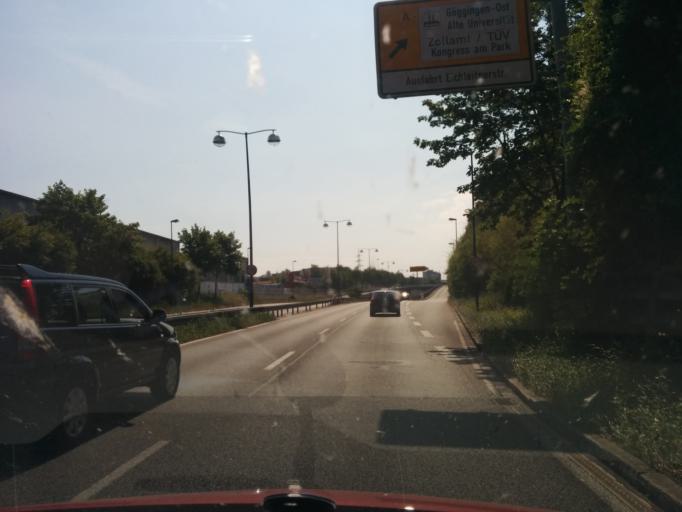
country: DE
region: Bavaria
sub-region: Swabia
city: Augsburg
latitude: 48.3452
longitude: 10.8822
